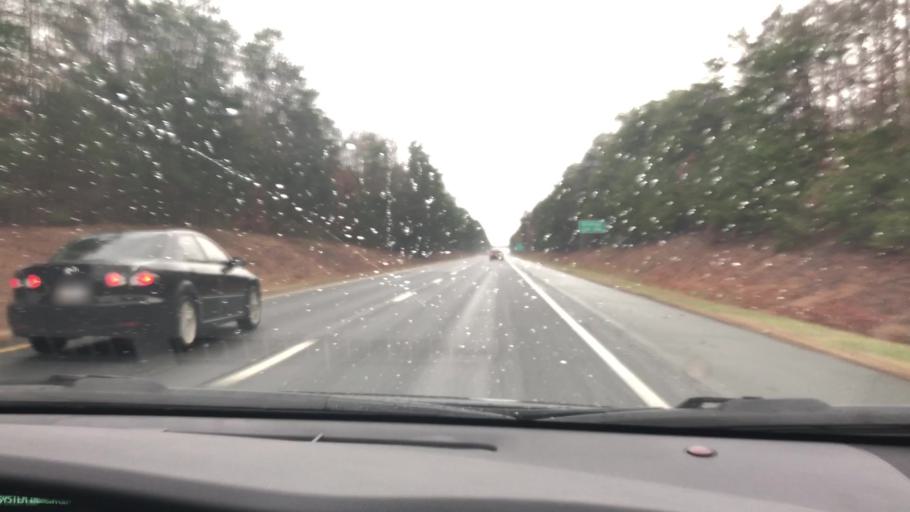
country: US
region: Virginia
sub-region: Fluvanna County
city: Palmyra
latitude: 37.9658
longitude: -78.1853
